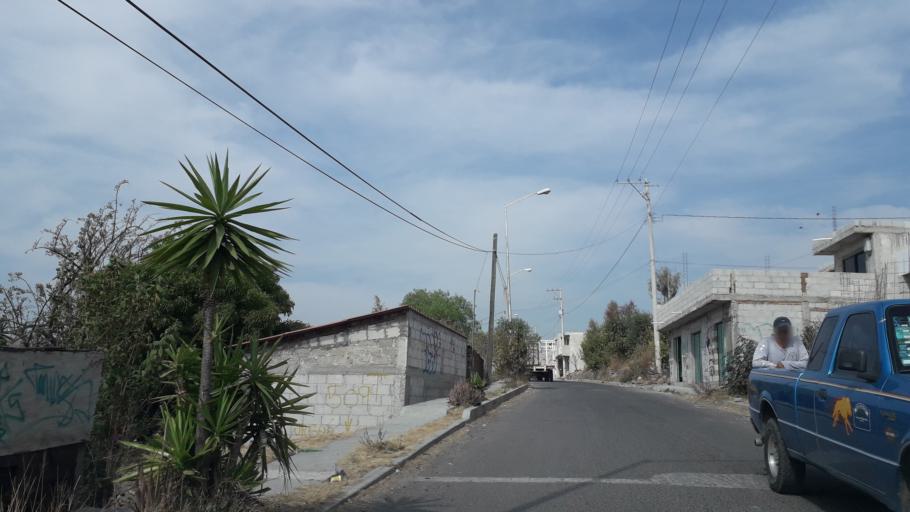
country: MX
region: Puebla
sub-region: Puebla
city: San Andres Azumiatla
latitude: 18.9077
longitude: -98.2464
